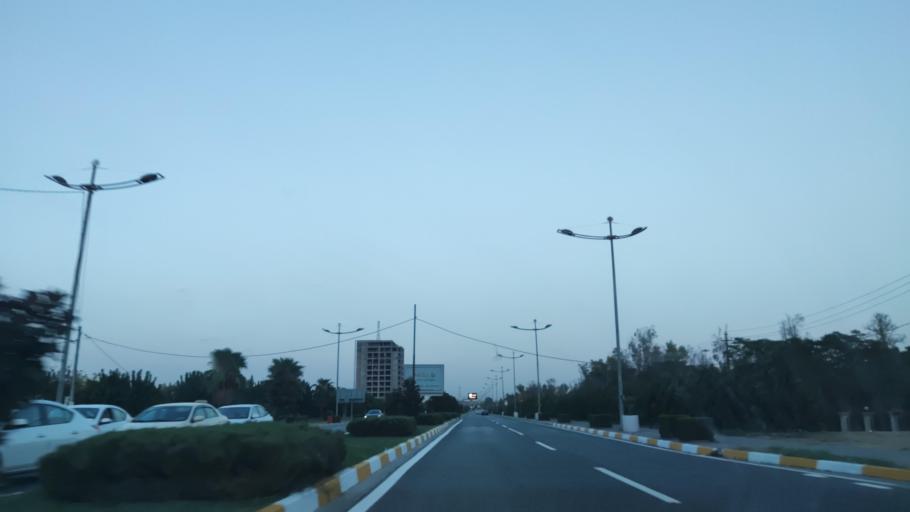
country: IQ
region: Arbil
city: Erbil
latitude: 36.1997
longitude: 43.9810
